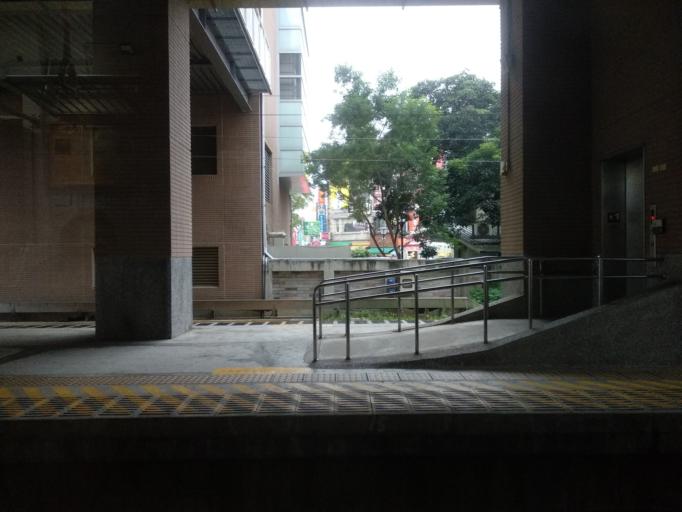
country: TW
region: Taiwan
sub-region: Hsinchu
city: Zhubei
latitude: 24.9029
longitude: 121.0438
